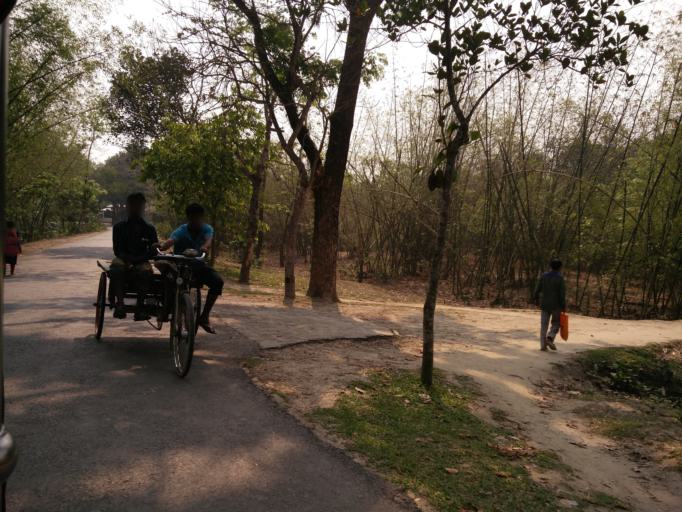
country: BD
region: Dhaka
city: Muktagacha
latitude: 24.9073
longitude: 90.2016
